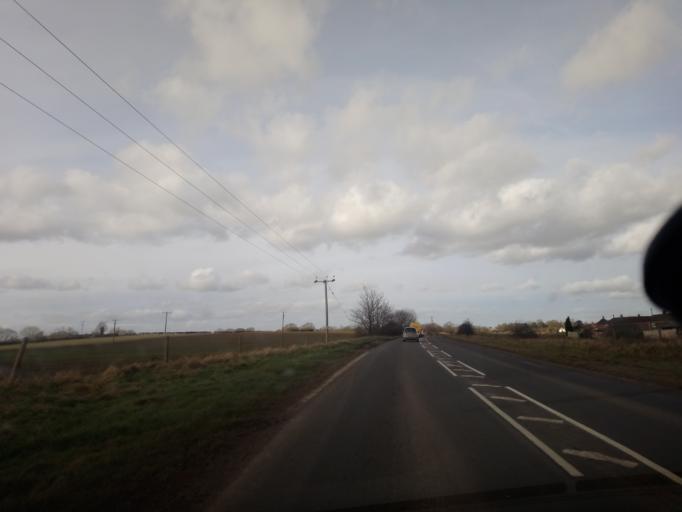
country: GB
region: England
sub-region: Telford and Wrekin
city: Eyton upon the Weald Moors
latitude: 52.7750
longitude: -2.5523
